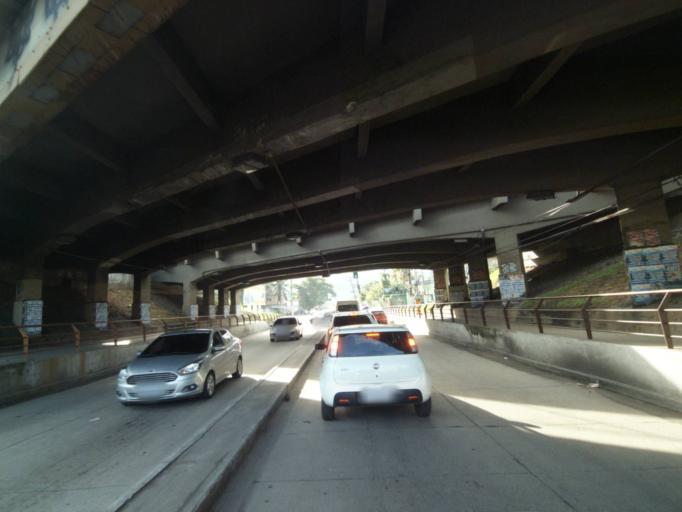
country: BR
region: Rio de Janeiro
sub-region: Nilopolis
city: Nilopolis
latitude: -22.8609
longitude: -43.4525
